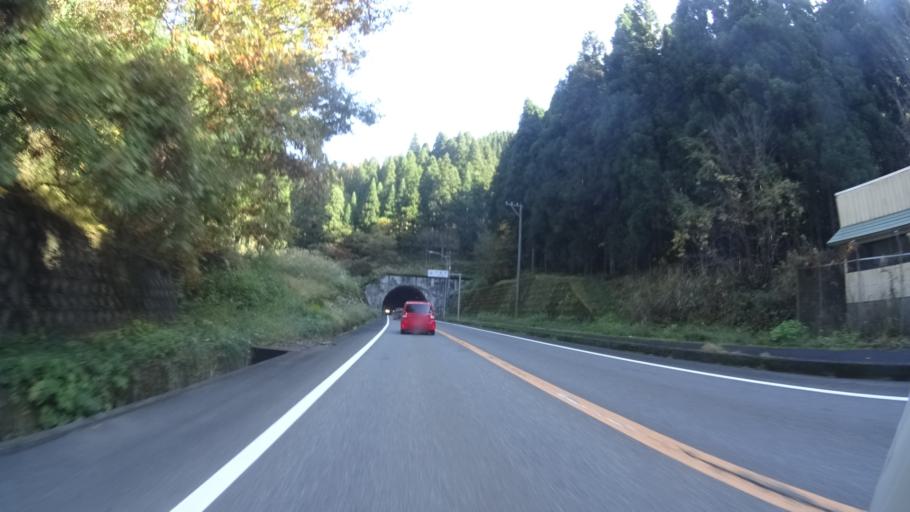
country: JP
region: Fukui
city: Ono
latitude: 35.9917
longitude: 136.4508
